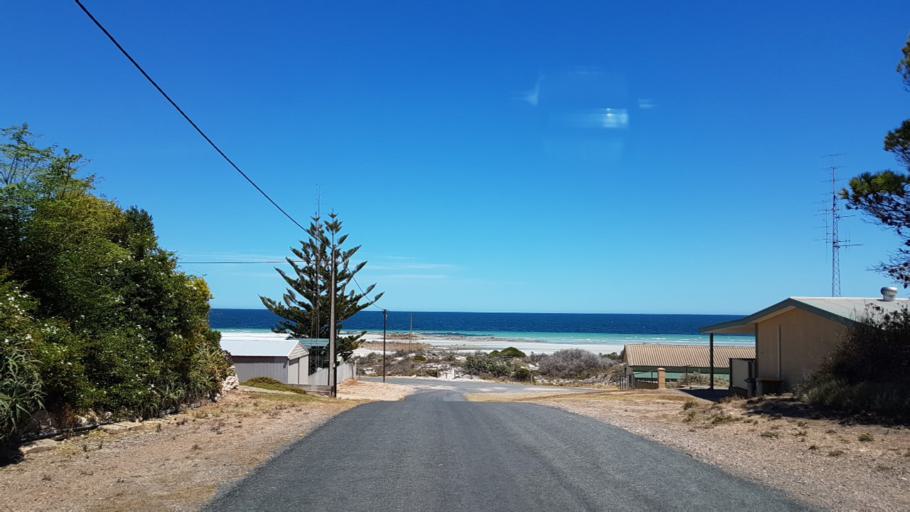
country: AU
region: South Australia
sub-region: Copper Coast
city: Wallaroo
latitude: -33.9006
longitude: 137.6297
